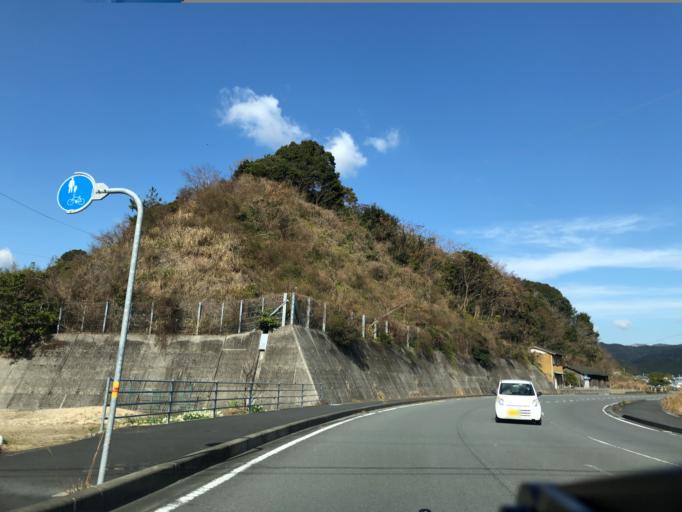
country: JP
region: Kochi
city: Sukumo
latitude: 32.9188
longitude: 132.7023
